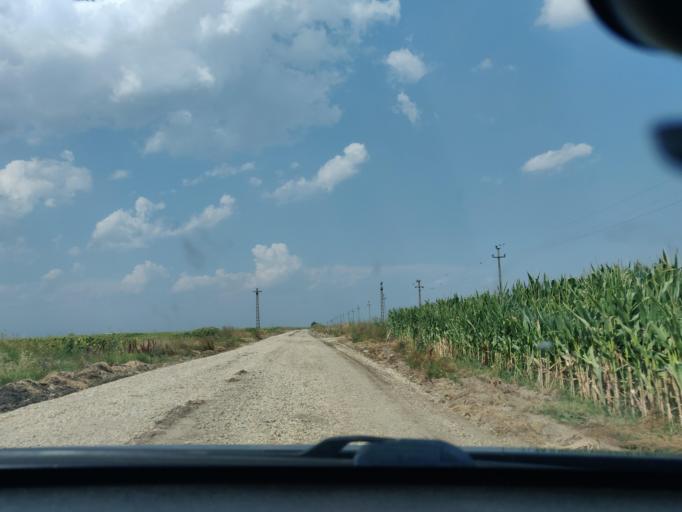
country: RO
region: Teleorman
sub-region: Comuna Sarbeni
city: Sarbeni
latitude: 44.4946
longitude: 25.3949
